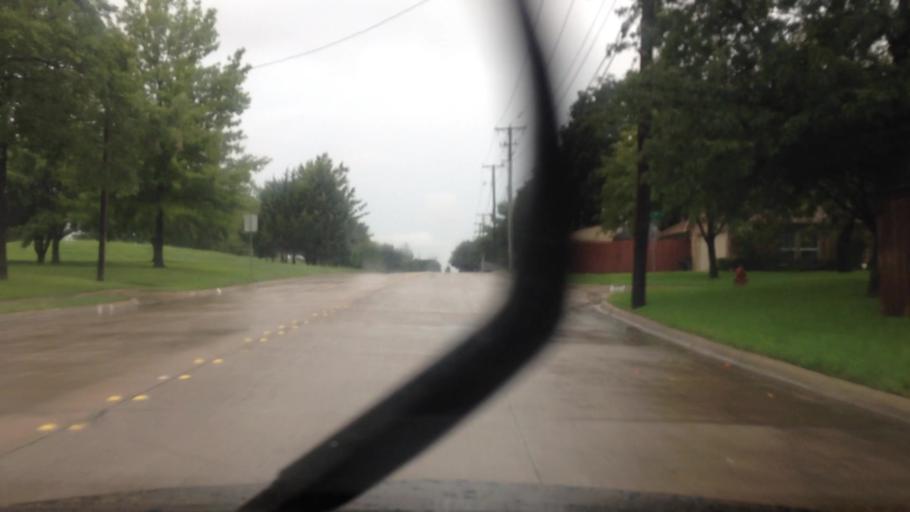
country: US
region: Texas
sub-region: Tarrant County
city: Watauga
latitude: 32.8898
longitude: -97.2291
